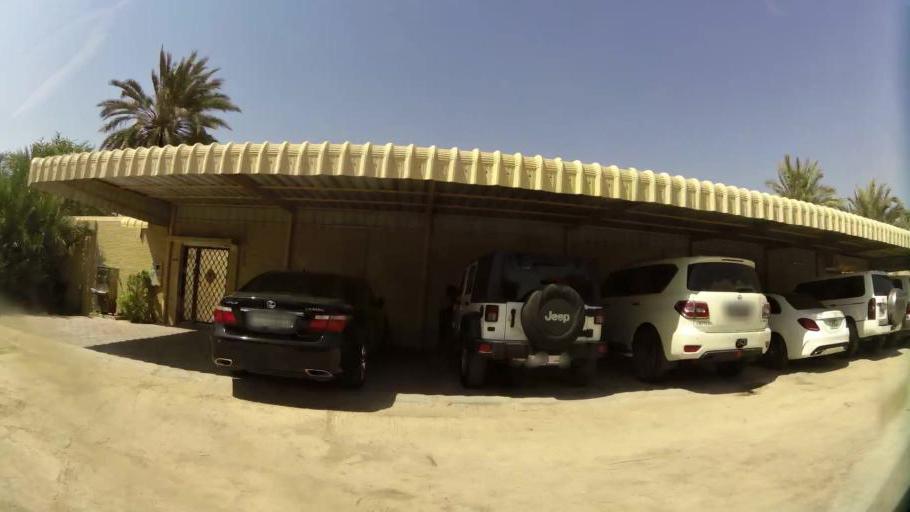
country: AE
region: Ajman
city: Ajman
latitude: 25.4132
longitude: 55.4784
